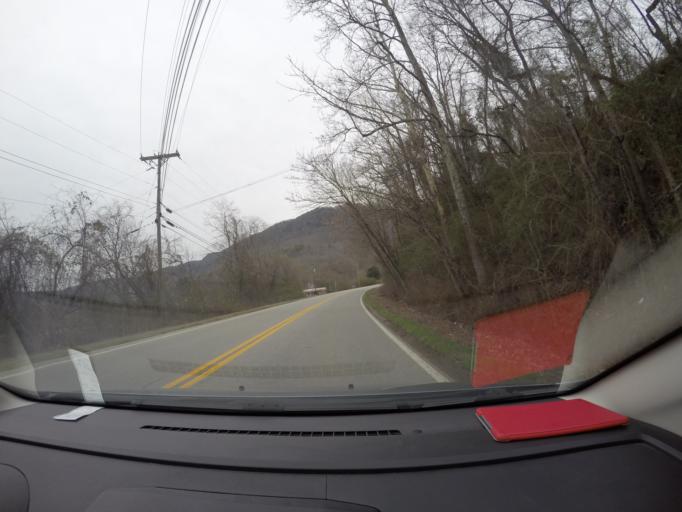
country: US
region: Tennessee
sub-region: Hamilton County
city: Signal Mountain
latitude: 35.1222
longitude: -85.3895
